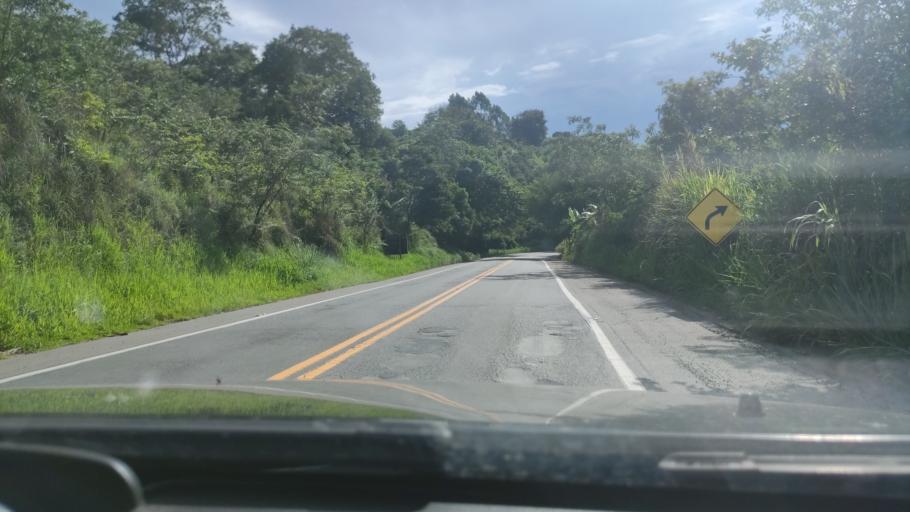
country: BR
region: Sao Paulo
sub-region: Aguas De Lindoia
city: Aguas de Lindoia
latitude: -22.5467
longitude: -46.6213
